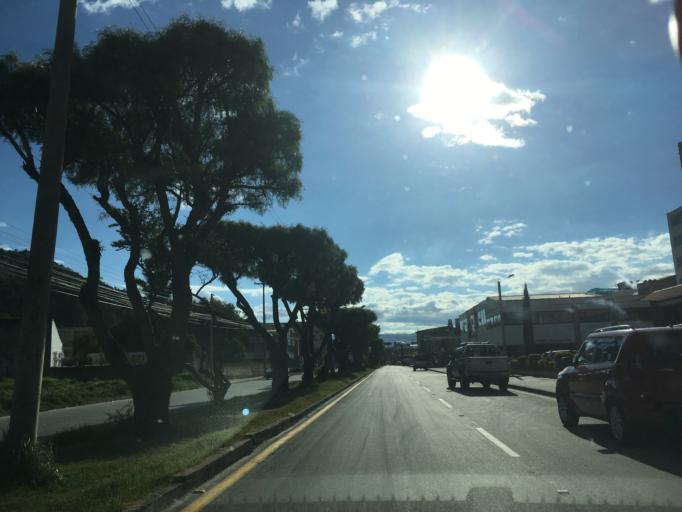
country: CO
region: Boyaca
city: Sogamoso
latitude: 5.7081
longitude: -72.9291
